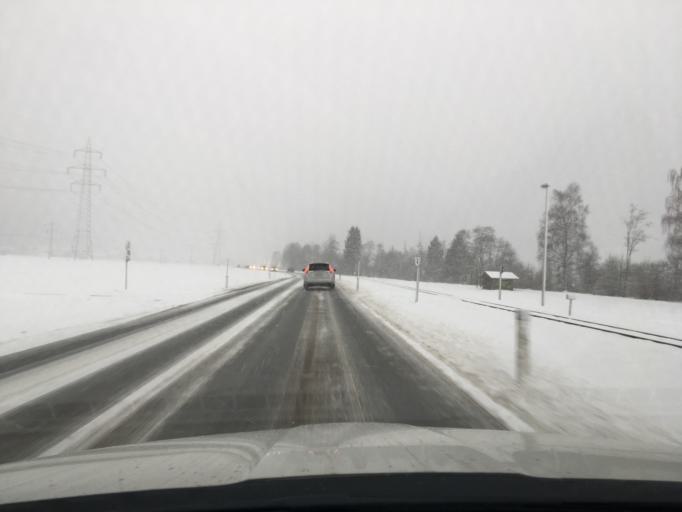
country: AT
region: Tyrol
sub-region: Politischer Bezirk Schwaz
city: Schwendau
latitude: 47.1863
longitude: 11.8663
